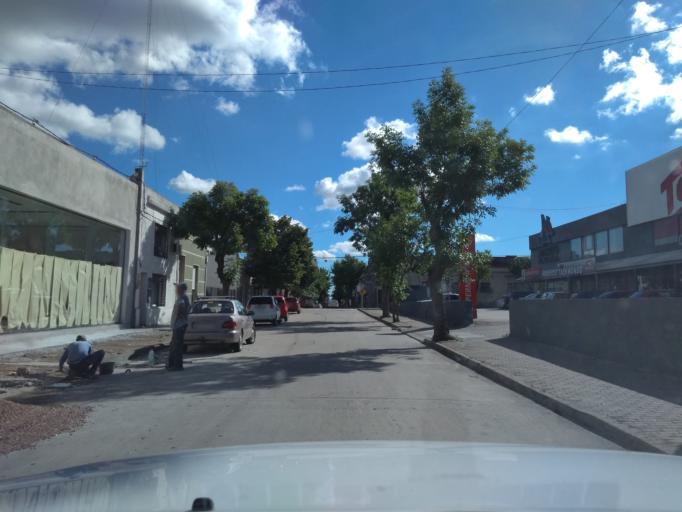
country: UY
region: Florida
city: Florida
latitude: -34.0960
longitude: -56.2143
